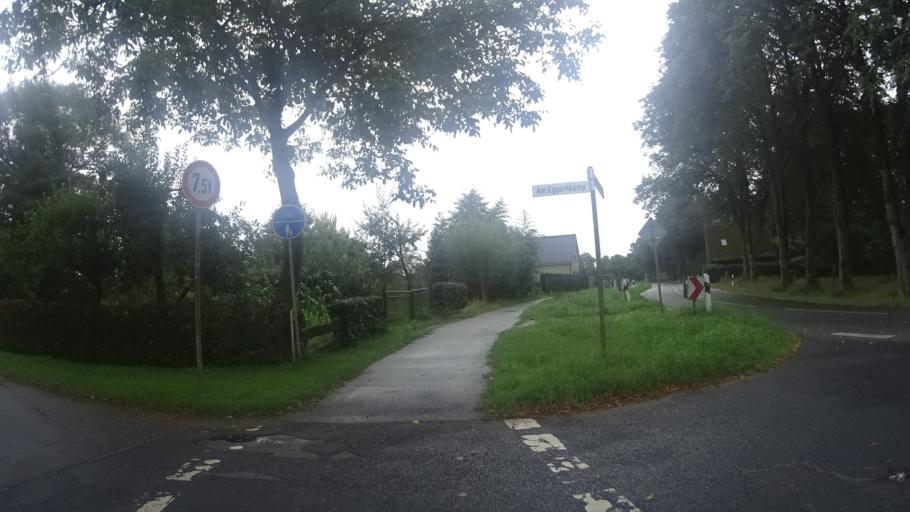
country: DE
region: Schleswig-Holstein
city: Seeth-Ekholt
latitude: 53.7574
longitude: 9.7310
